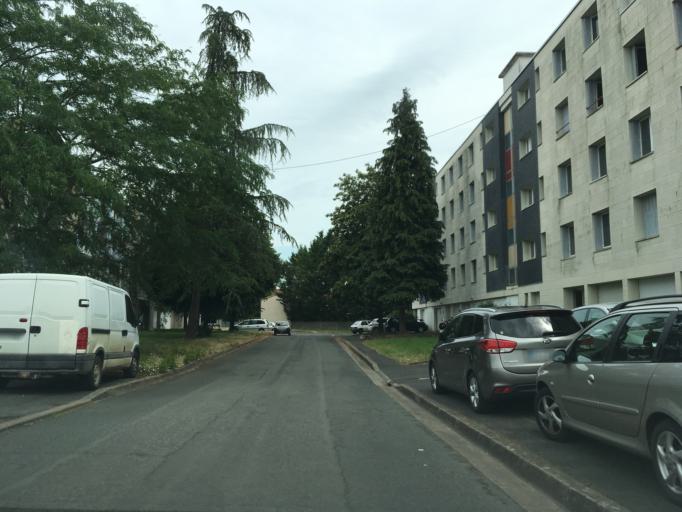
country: FR
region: Poitou-Charentes
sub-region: Departement des Deux-Sevres
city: Niort
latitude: 46.3151
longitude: -0.4771
